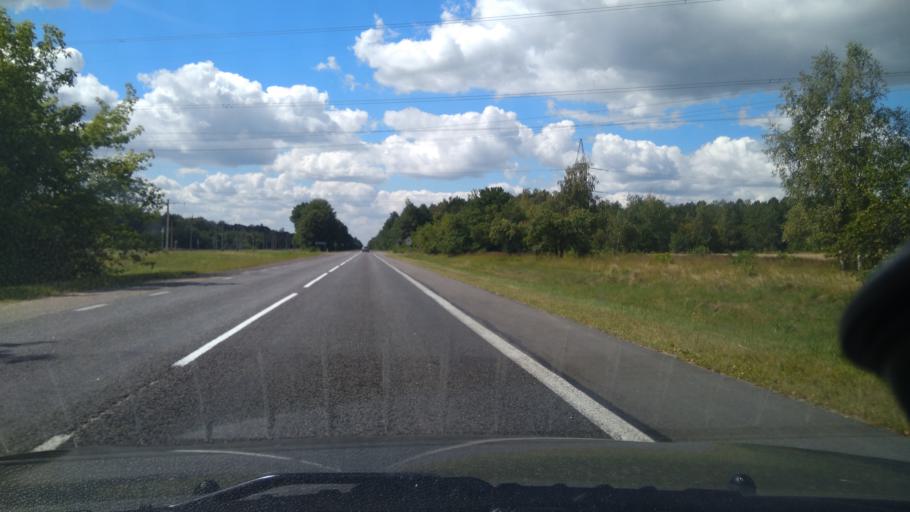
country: BY
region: Brest
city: Nyakhachava
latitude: 52.6750
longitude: 25.2683
